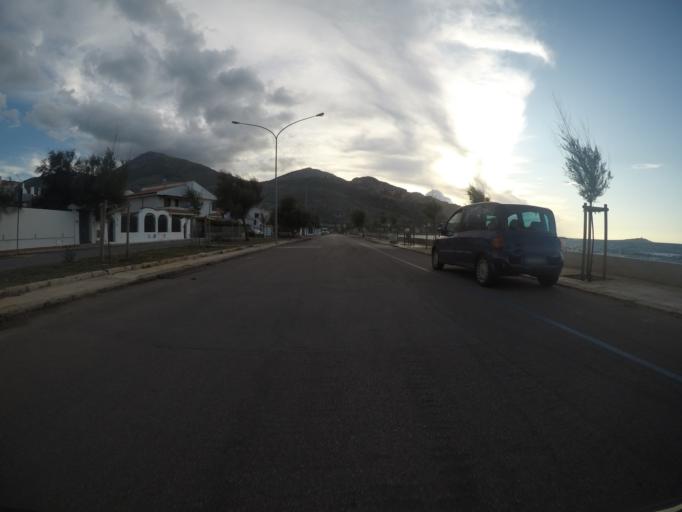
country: IT
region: Sicily
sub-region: Palermo
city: Isola delle Femmine
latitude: 38.2034
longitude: 13.2787
